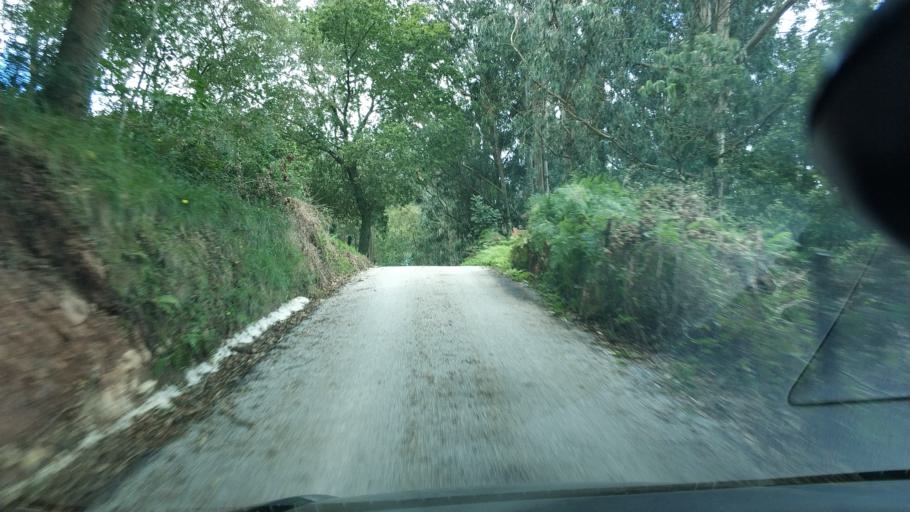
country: ES
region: Cantabria
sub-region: Provincia de Cantabria
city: Santa Maria de Cayon
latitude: 43.2914
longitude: -3.8549
